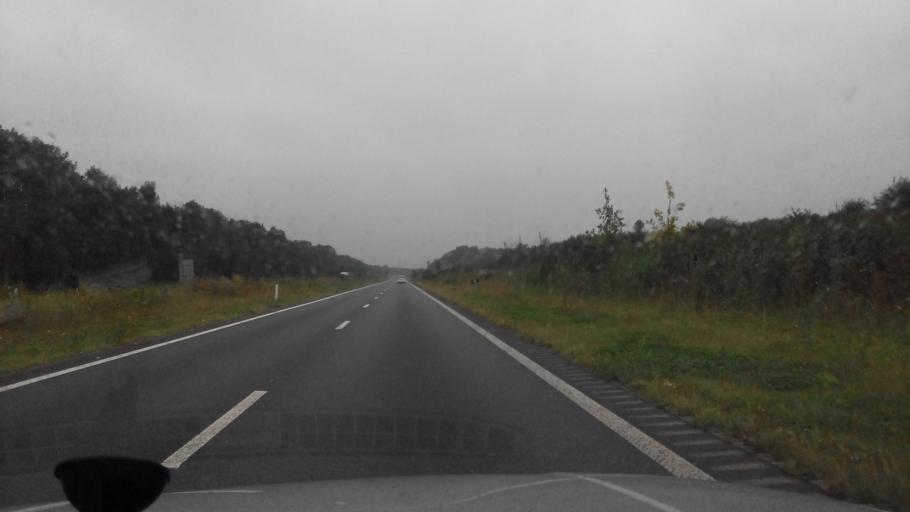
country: NL
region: Flevoland
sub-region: Gemeente Zeewolde
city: Zeewolde
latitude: 52.3438
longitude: 5.4947
